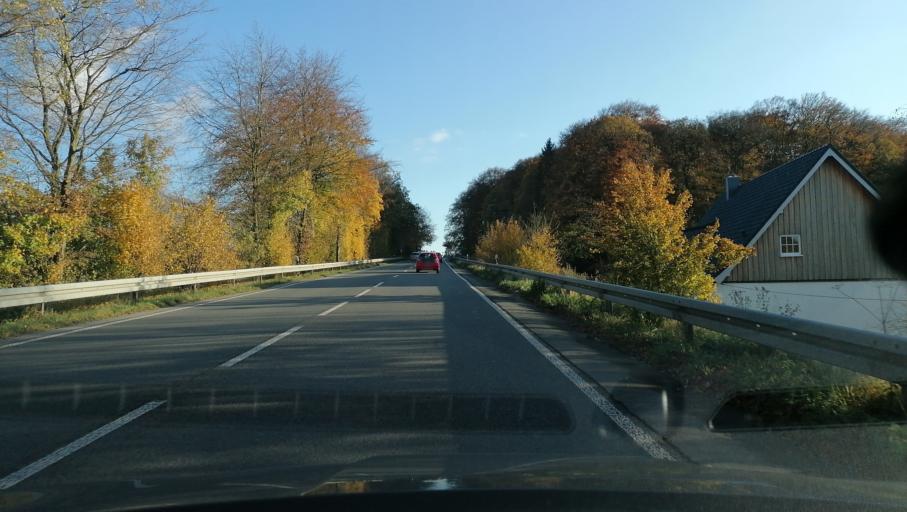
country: DE
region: North Rhine-Westphalia
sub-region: Regierungsbezirk Arnsberg
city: Schwelm
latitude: 51.2700
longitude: 7.3209
